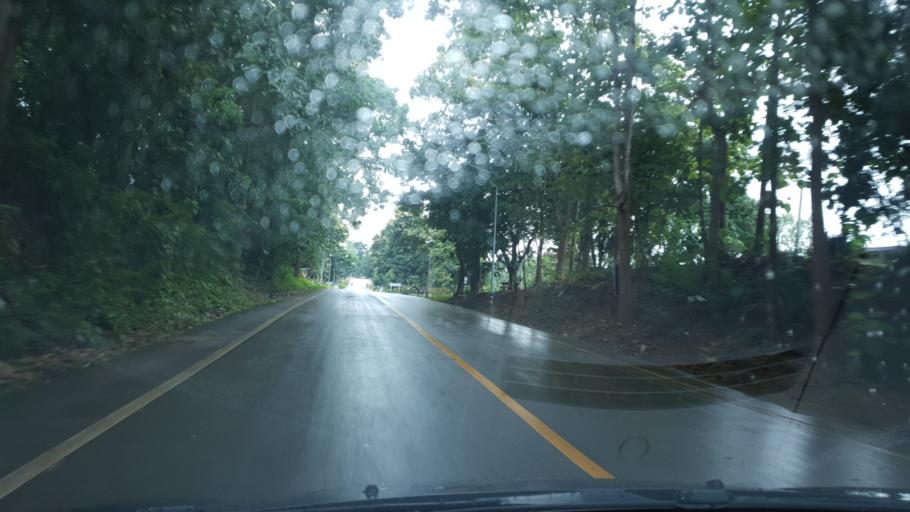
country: TH
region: Mae Hong Son
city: Mae La Noi
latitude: 18.5318
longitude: 97.9347
